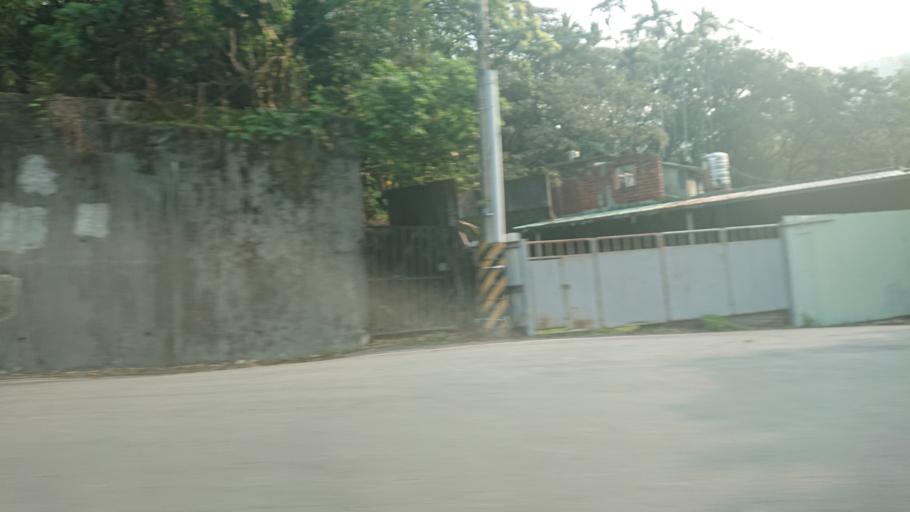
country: TW
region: Taiwan
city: Daxi
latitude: 24.8702
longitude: 121.4116
